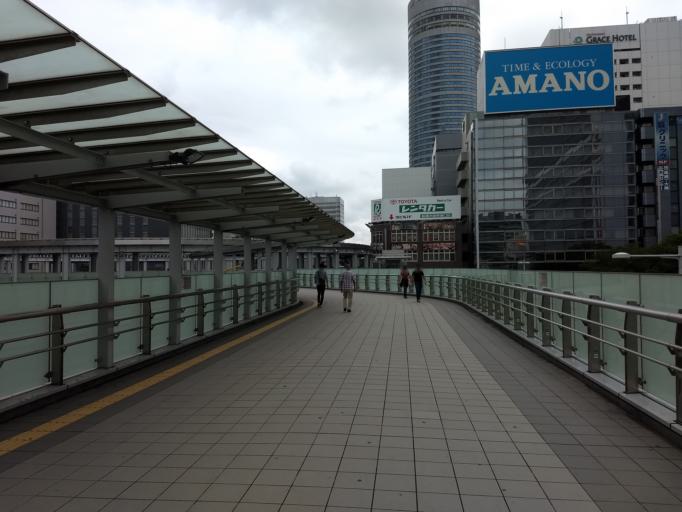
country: JP
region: Kanagawa
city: Yokohama
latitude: 35.5083
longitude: 139.6171
